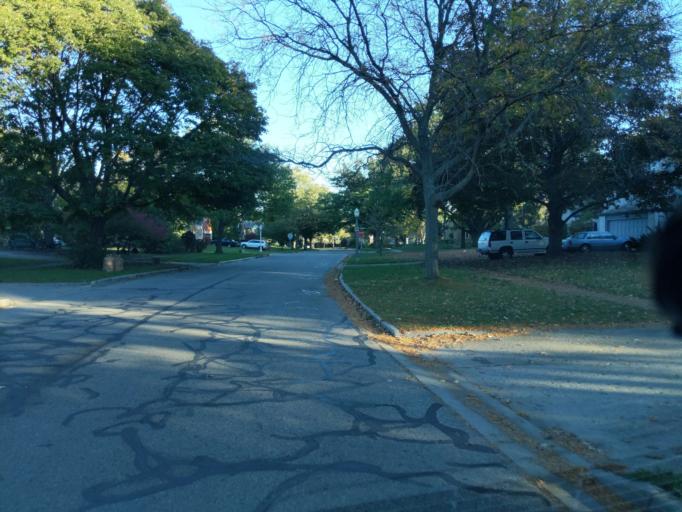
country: US
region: Michigan
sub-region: Ingham County
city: Lansing
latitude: 42.7310
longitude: -84.5763
